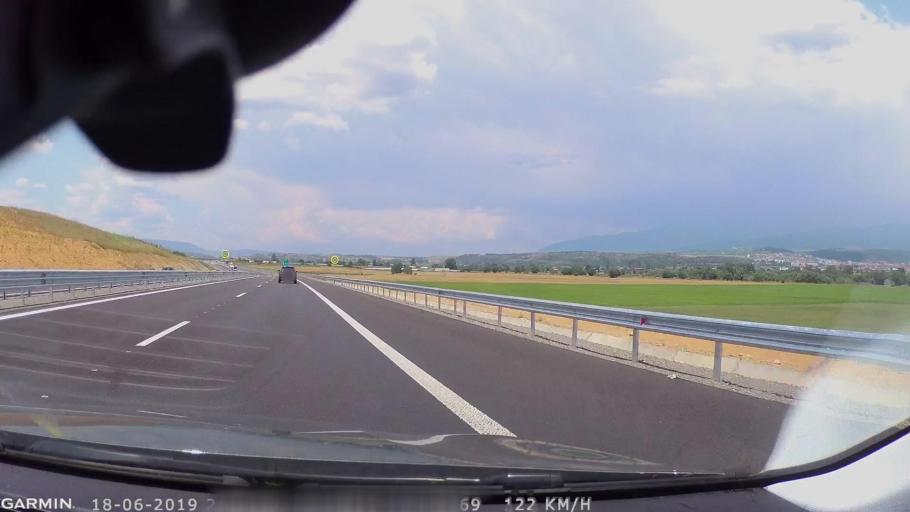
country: BG
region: Blagoevgrad
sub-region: Obshtina Blagoevgrad
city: Blagoevgrad
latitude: 41.9805
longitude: 23.0635
